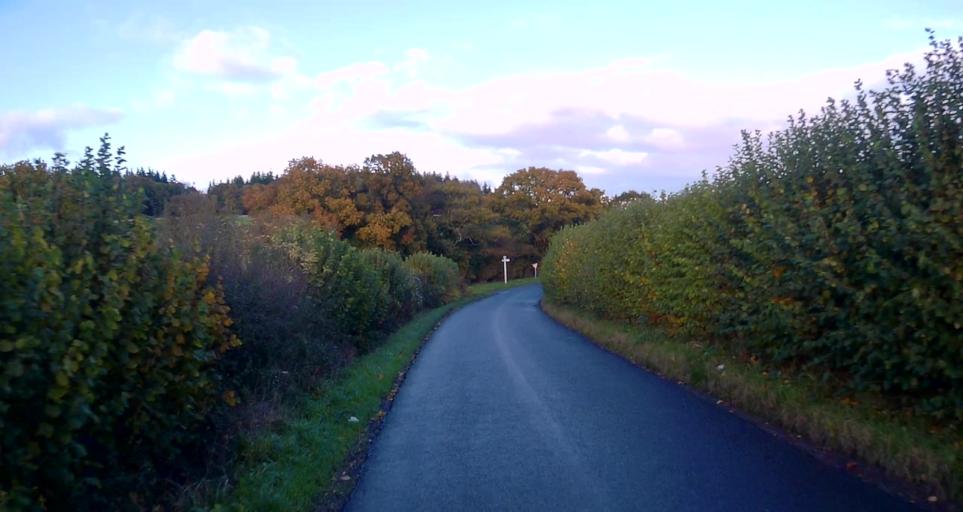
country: GB
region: England
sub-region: Hampshire
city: Basingstoke
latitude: 51.1900
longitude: -1.0771
